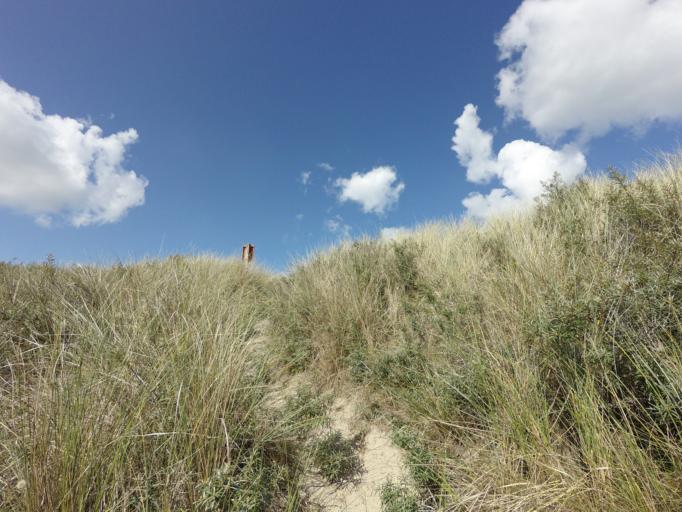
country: NL
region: Friesland
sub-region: Gemeente Terschelling
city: West-Terschelling
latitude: 53.3904
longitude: 5.2032
